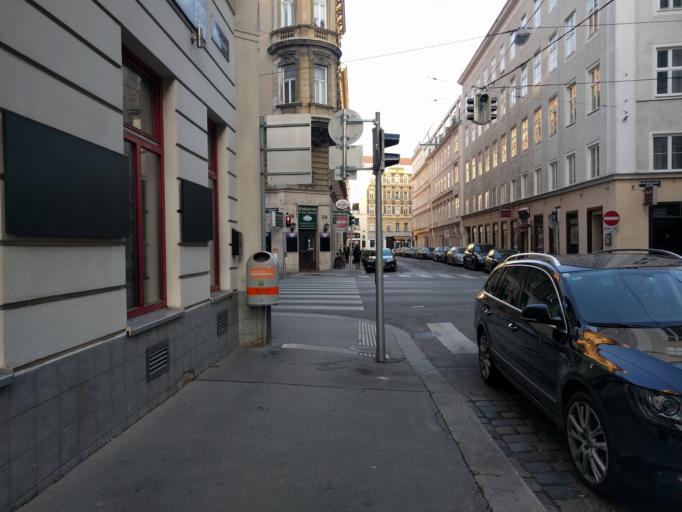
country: AT
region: Vienna
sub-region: Wien Stadt
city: Vienna
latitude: 48.2190
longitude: 16.3607
